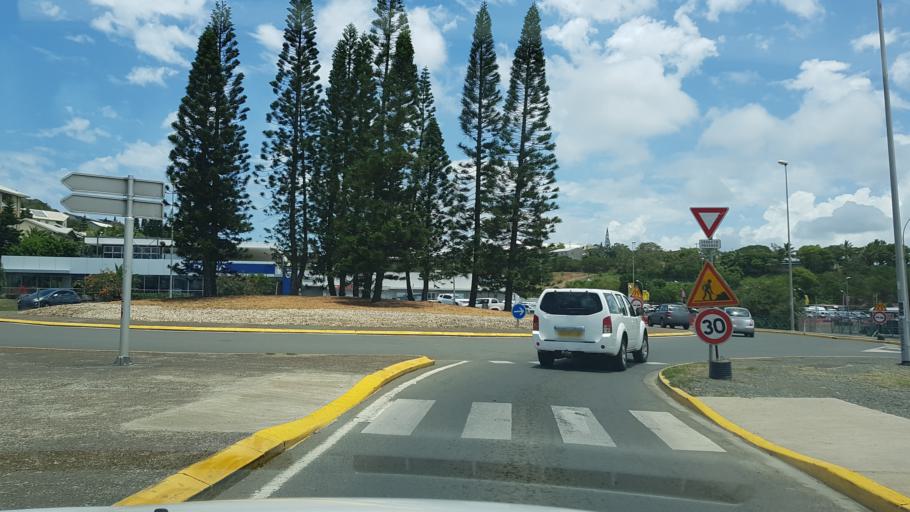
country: NC
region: South Province
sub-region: Noumea
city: Noumea
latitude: -22.2607
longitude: 166.4700
